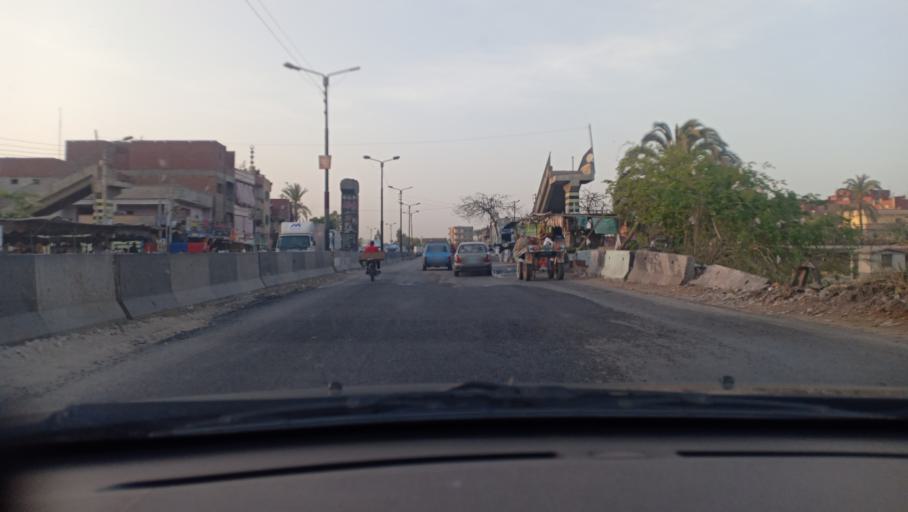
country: EG
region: Muhafazat al Gharbiyah
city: Zifta
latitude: 30.6704
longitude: 31.2858
